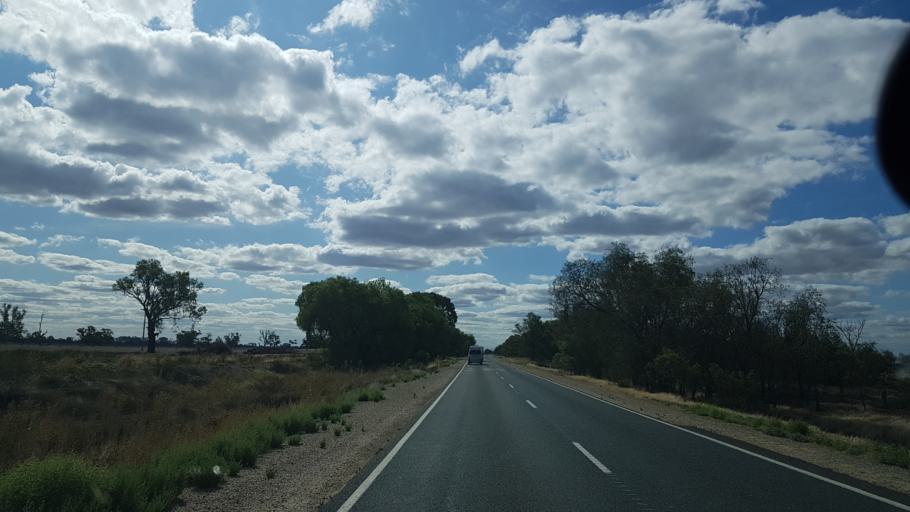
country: AU
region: Victoria
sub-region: Swan Hill
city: Swan Hill
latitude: -35.7983
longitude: 143.9536
